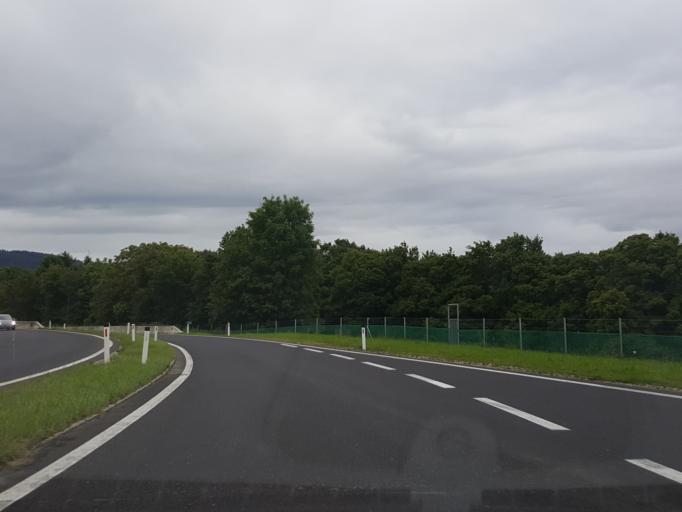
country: AT
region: Upper Austria
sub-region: Politischer Bezirk Vocklabruck
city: Seewalchen
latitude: 47.9529
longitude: 13.5940
